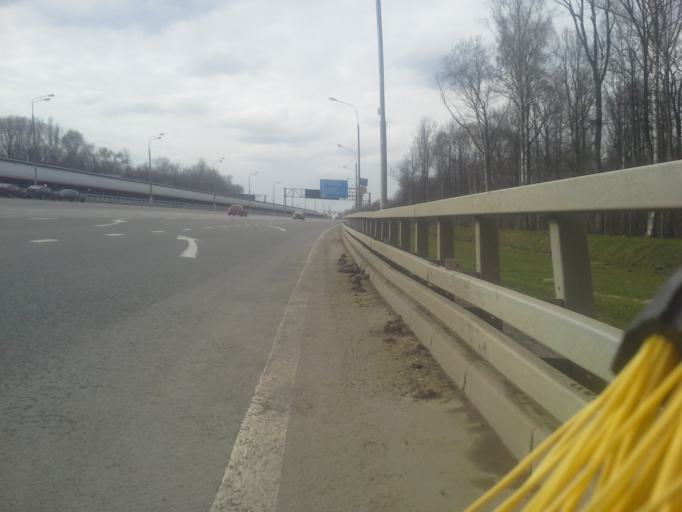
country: RU
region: Moskovskaya
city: Kommunarka
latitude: 55.5770
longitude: 37.4501
